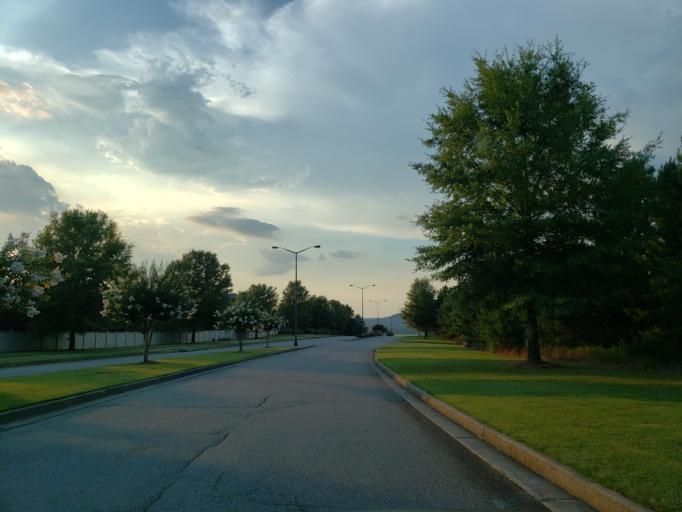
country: US
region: Georgia
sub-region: Bartow County
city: Cartersville
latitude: 34.1105
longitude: -84.8212
